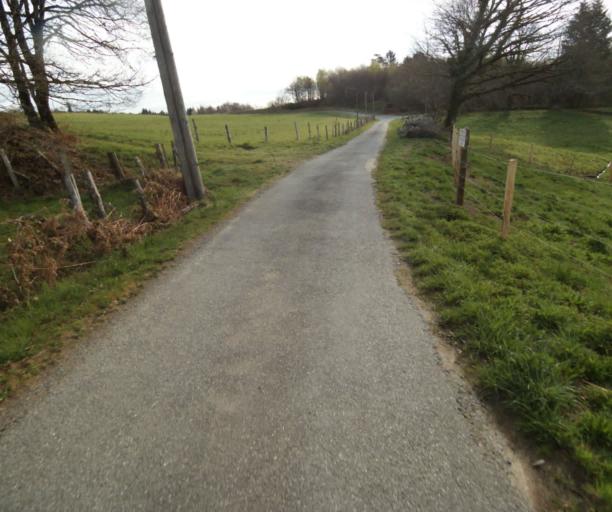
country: FR
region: Limousin
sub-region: Departement de la Correze
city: Correze
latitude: 45.3642
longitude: 1.8564
